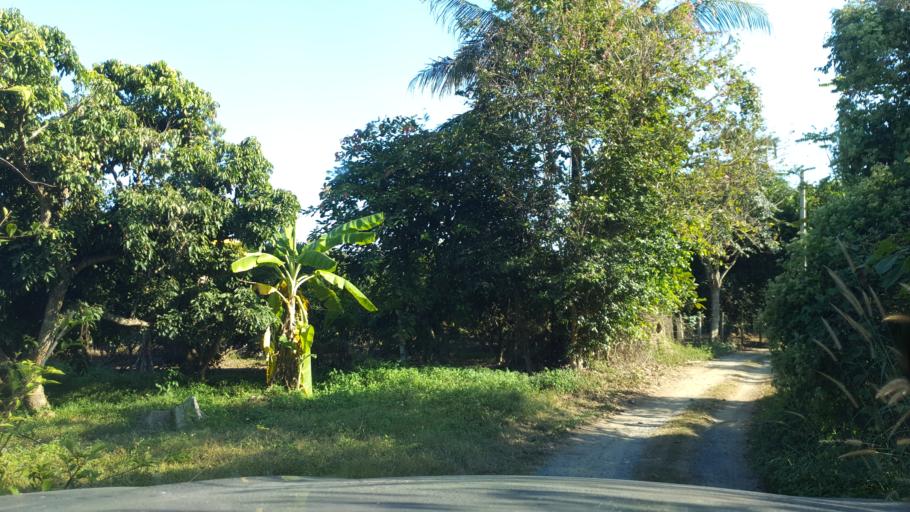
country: TH
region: Chiang Mai
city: Mae On
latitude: 18.7271
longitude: 99.1953
